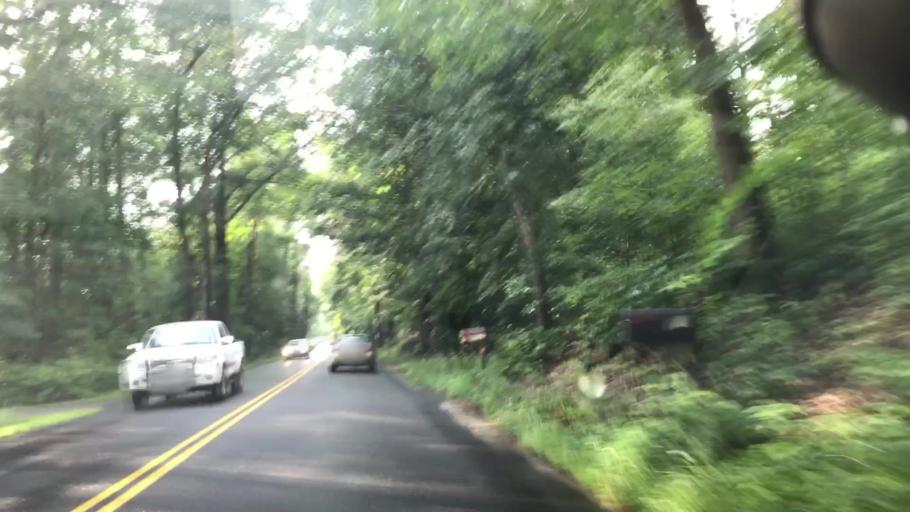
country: US
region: New Hampshire
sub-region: Hillsborough County
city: Milford
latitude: 42.8443
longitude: -71.6082
